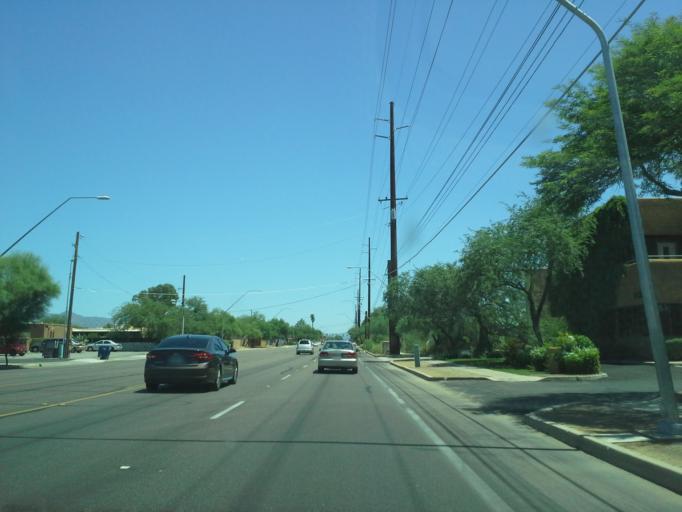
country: US
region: Arizona
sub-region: Pima County
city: Catalina Foothills
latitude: 32.2647
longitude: -110.9500
